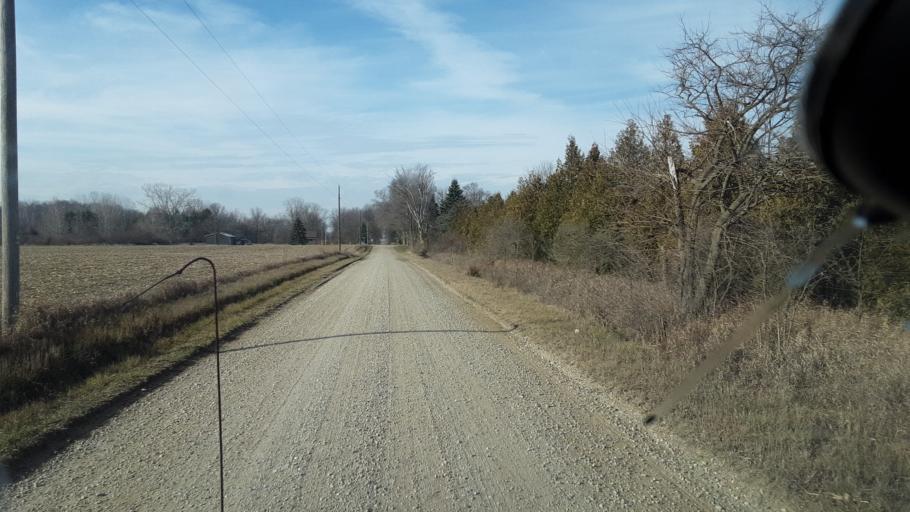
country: US
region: Ohio
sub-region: Defiance County
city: Hicksville
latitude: 41.2706
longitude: -84.8248
